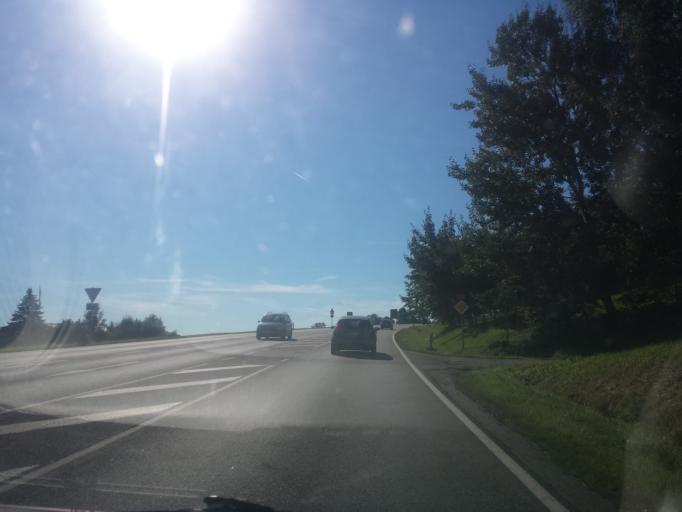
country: DE
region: Bavaria
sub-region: Lower Bavaria
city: Viechtach
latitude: 49.0776
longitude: 12.8753
